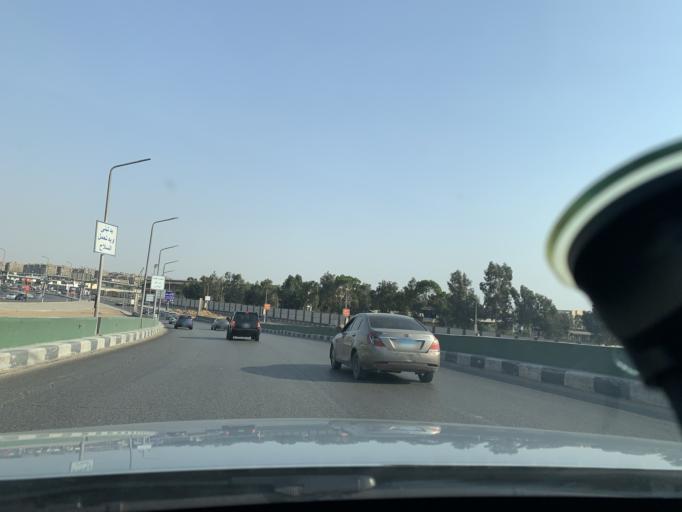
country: EG
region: Muhafazat al Qalyubiyah
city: Al Khankah
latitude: 30.1152
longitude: 31.3666
